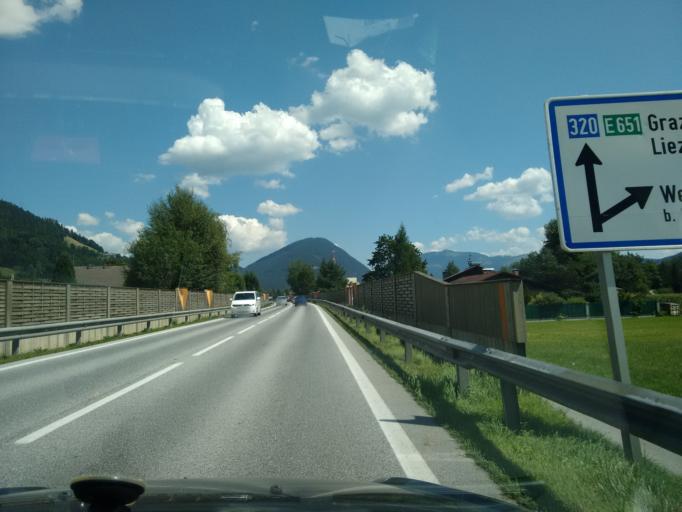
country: AT
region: Styria
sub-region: Politischer Bezirk Liezen
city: Weissenbach bei Liezen
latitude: 47.5669
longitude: 14.2030
